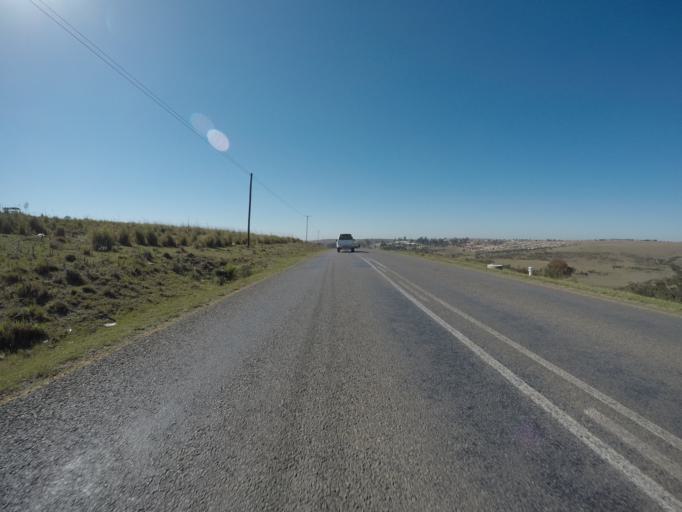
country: ZA
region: Eastern Cape
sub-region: OR Tambo District Municipality
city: Mthatha
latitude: -31.8037
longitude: 28.7528
